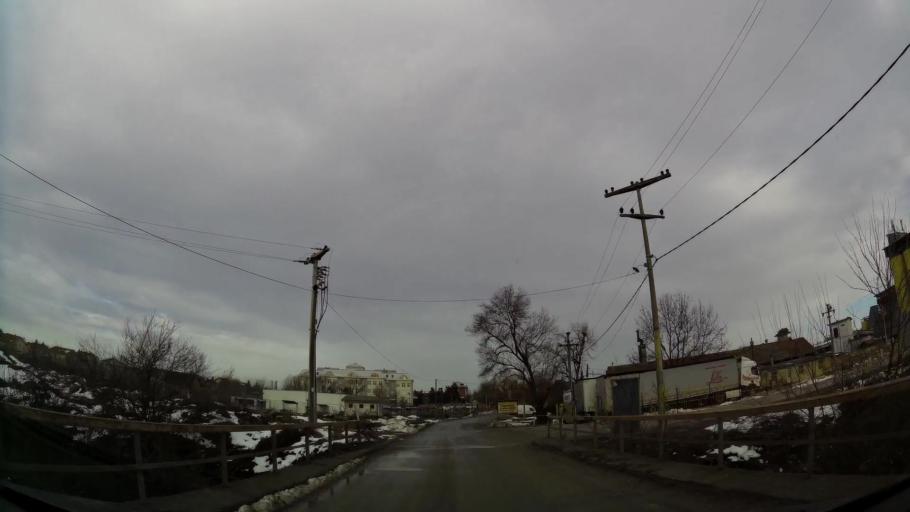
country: RS
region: Central Serbia
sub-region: Belgrade
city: Surcin
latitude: 44.7876
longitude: 20.2712
